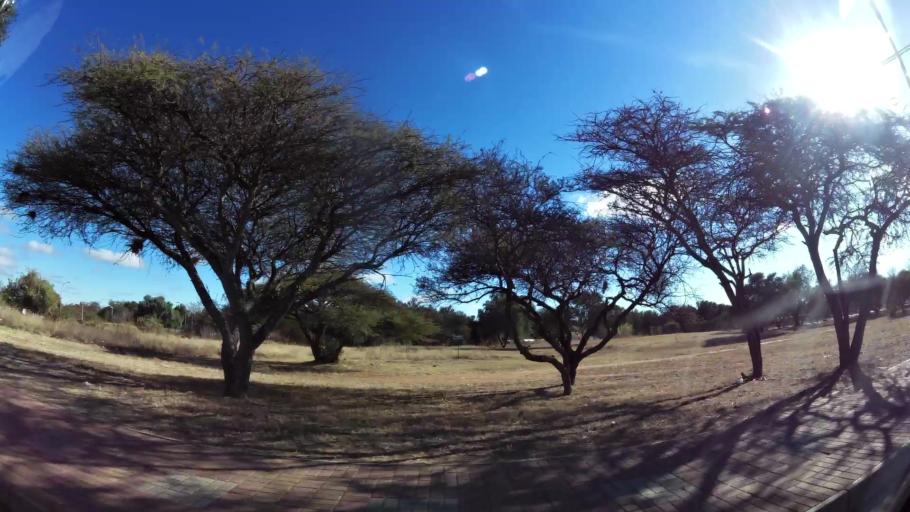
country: ZA
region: Limpopo
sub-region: Capricorn District Municipality
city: Polokwane
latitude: -23.9215
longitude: 29.4636
